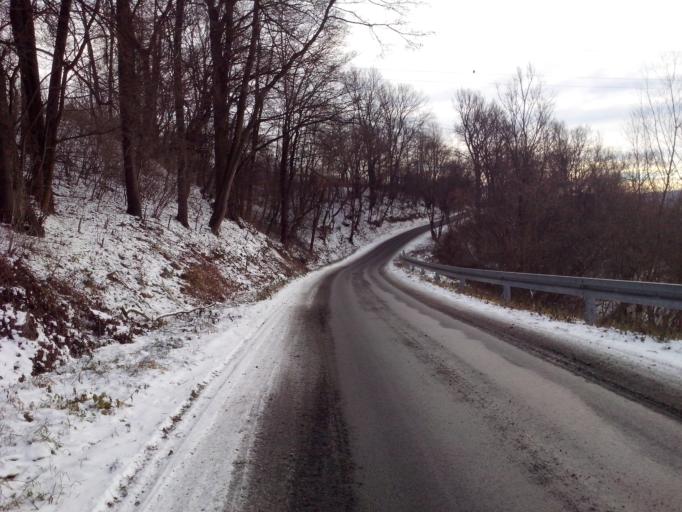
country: PL
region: Subcarpathian Voivodeship
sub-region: Powiat strzyzowski
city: Strzyzow
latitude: 49.8629
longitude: 21.7999
